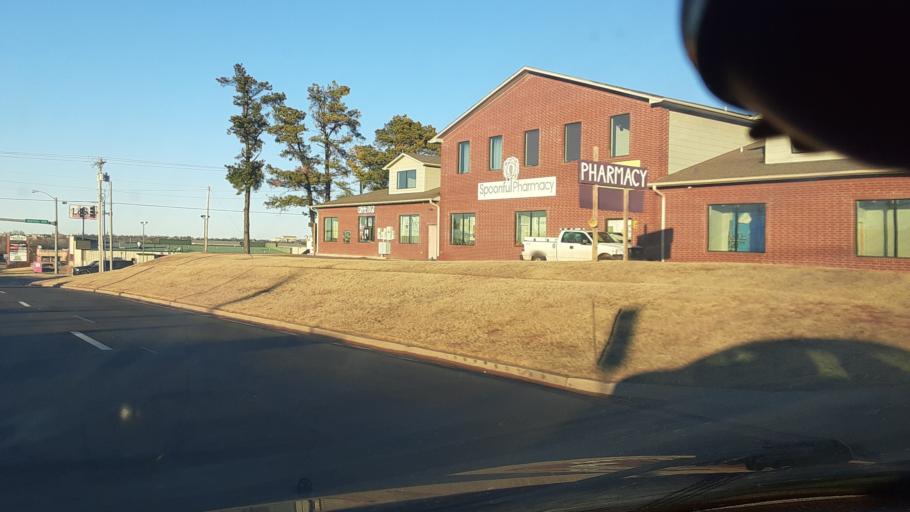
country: US
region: Oklahoma
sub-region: Logan County
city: Guthrie
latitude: 35.8555
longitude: -97.4254
